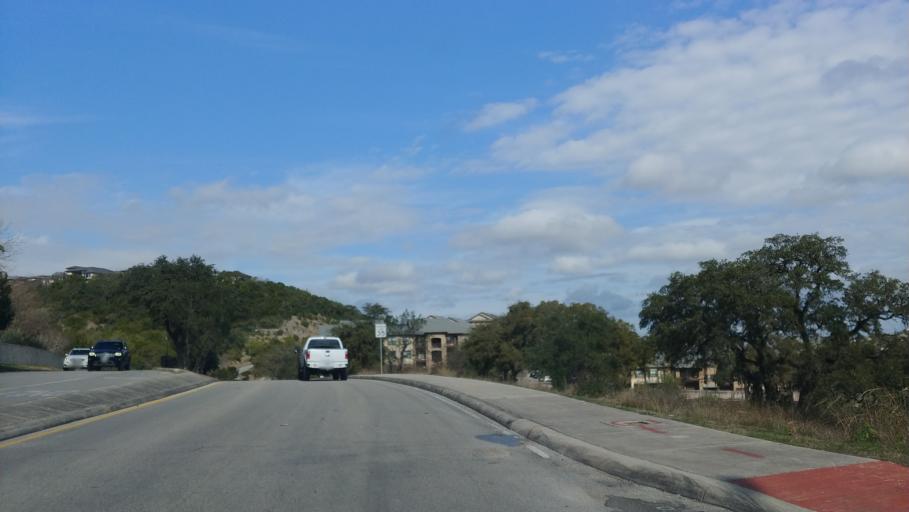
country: US
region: Texas
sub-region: Bexar County
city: Cross Mountain
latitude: 29.6199
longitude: -98.6113
